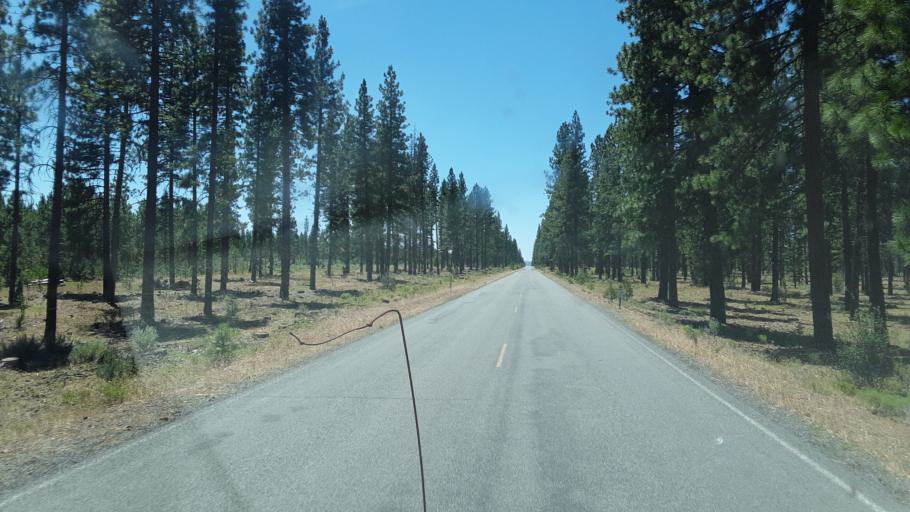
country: US
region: California
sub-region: Siskiyou County
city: Tulelake
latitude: 41.4083
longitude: -121.1804
